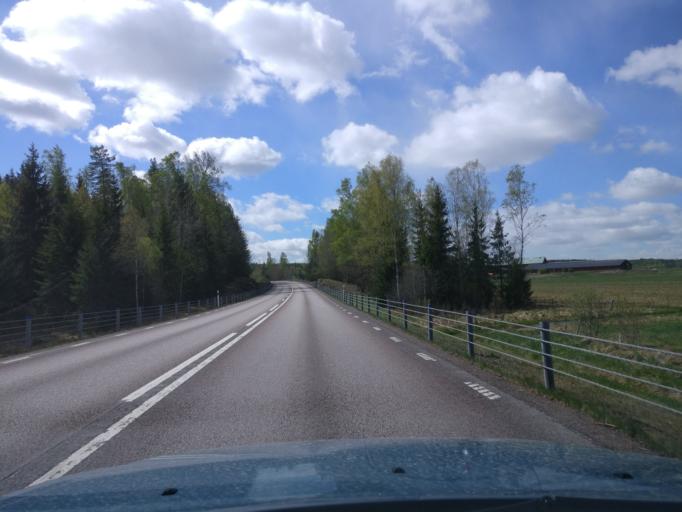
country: SE
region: Vaermland
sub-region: Karlstads Kommun
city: Molkom
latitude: 59.5423
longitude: 13.6259
